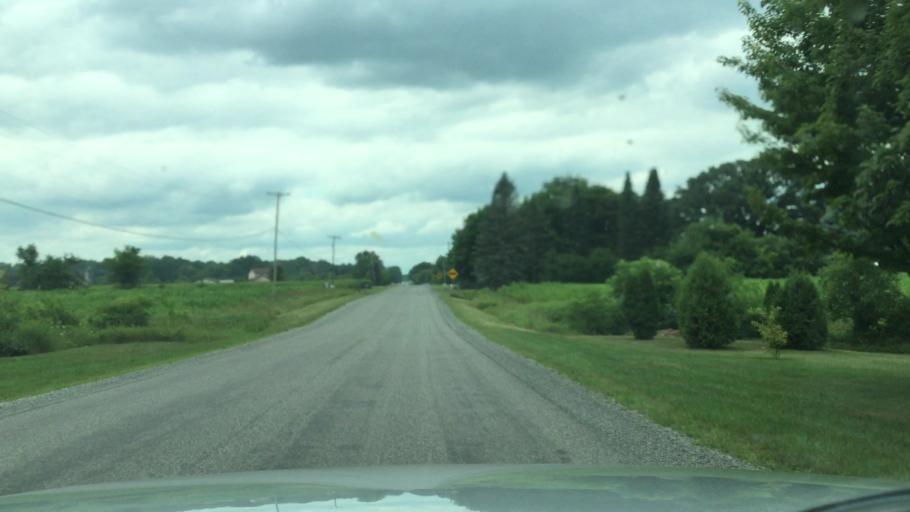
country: US
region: Michigan
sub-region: Saginaw County
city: Burt
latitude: 43.2500
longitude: -83.8639
